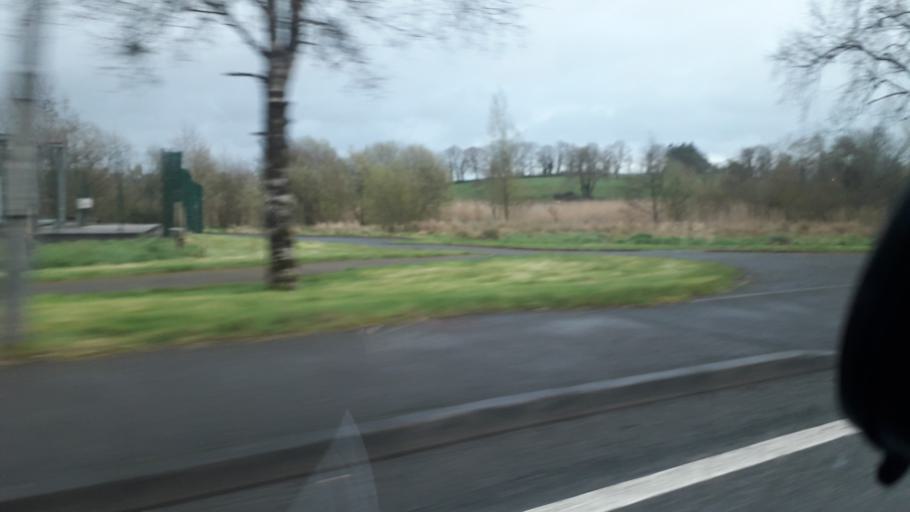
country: IE
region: Connaught
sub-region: County Leitrim
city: Carrick-on-Shannon
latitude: 53.9442
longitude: -8.0865
